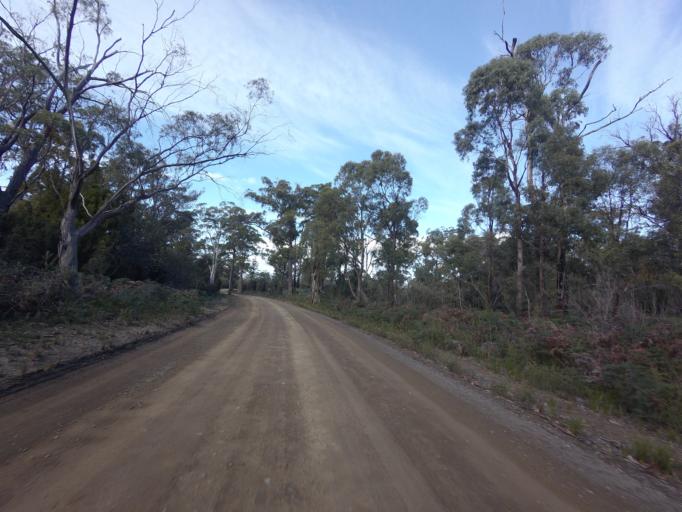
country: AU
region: Tasmania
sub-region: Clarence
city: Sandford
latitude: -42.9859
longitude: 147.7126
